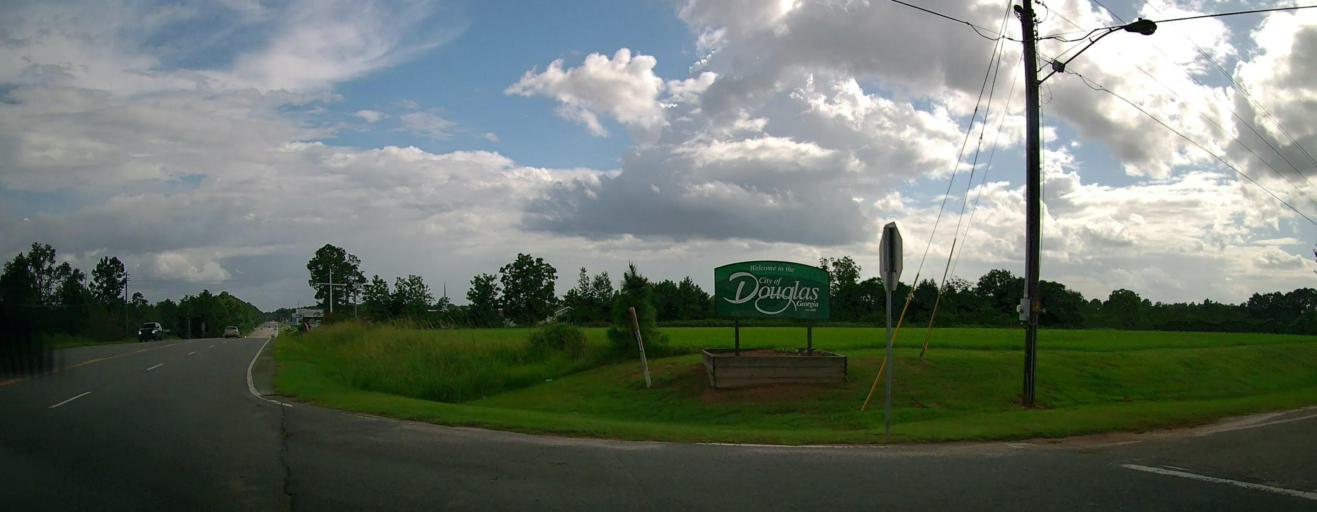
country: US
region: Georgia
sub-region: Coffee County
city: Douglas
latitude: 31.5463
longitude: -82.8518
